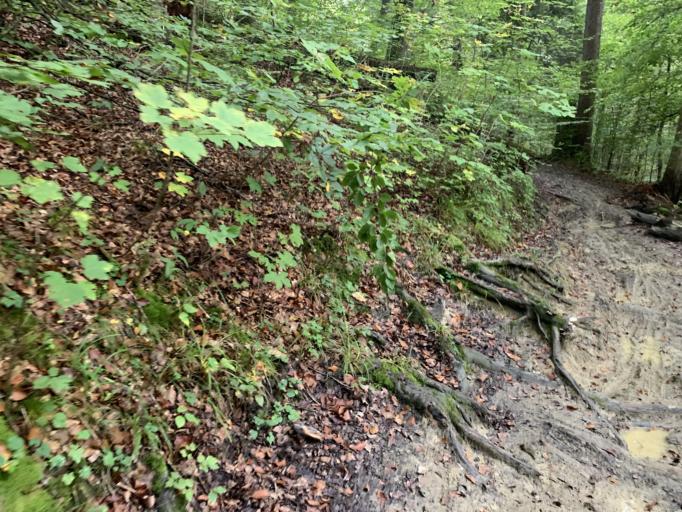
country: DE
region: Bavaria
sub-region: Upper Bavaria
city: Baierbrunn
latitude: 48.0051
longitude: 11.4827
